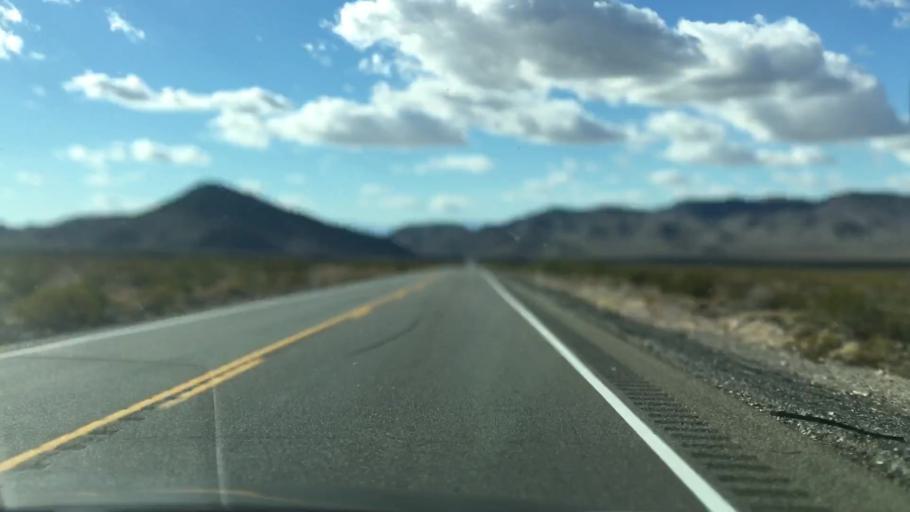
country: US
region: Nevada
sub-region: Nye County
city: Pahrump
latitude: 36.5942
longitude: -116.0192
